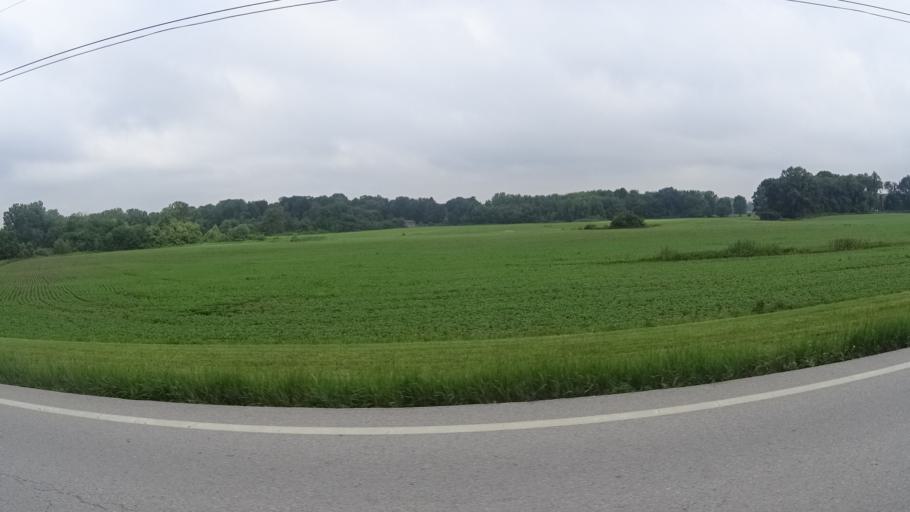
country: US
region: Ohio
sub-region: Erie County
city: Milan
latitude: 41.2972
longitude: -82.5252
